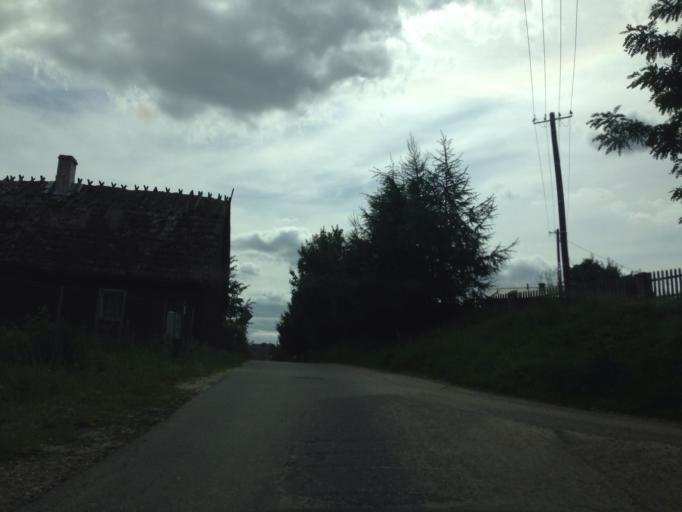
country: PL
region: Pomeranian Voivodeship
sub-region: Powiat koscierski
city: Lipusz
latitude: 54.0731
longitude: 17.7287
